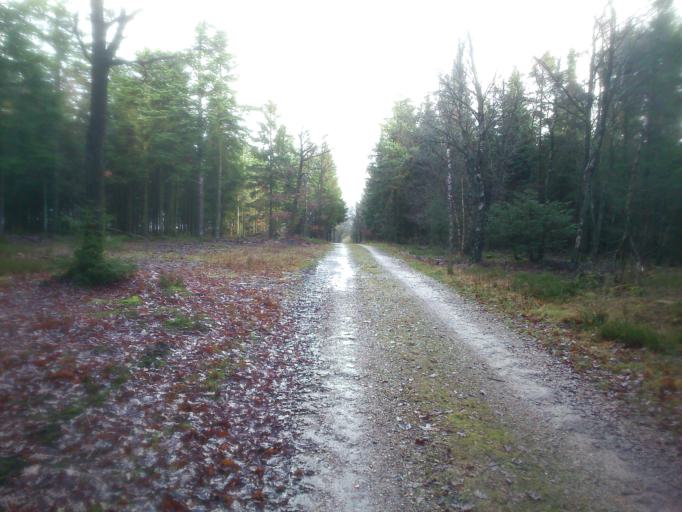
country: DK
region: Central Jutland
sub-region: Ringkobing-Skjern Kommune
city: Skjern
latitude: 55.9914
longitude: 8.4533
